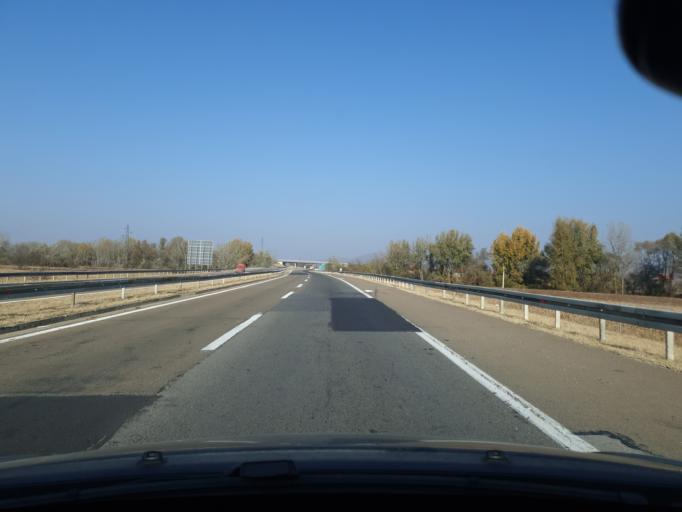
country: RS
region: Central Serbia
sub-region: Nisavski Okrug
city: Nis
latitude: 43.3361
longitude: 21.8154
